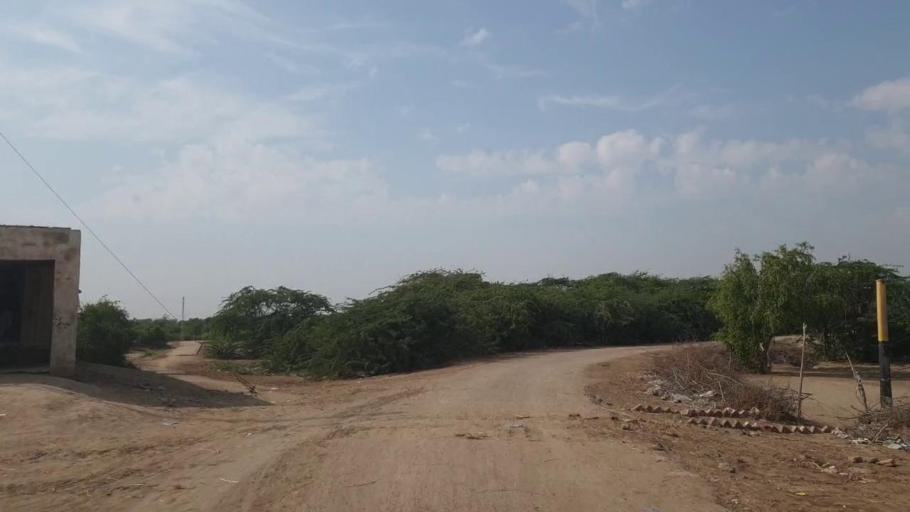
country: PK
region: Sindh
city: Digri
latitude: 25.0052
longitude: 69.0657
